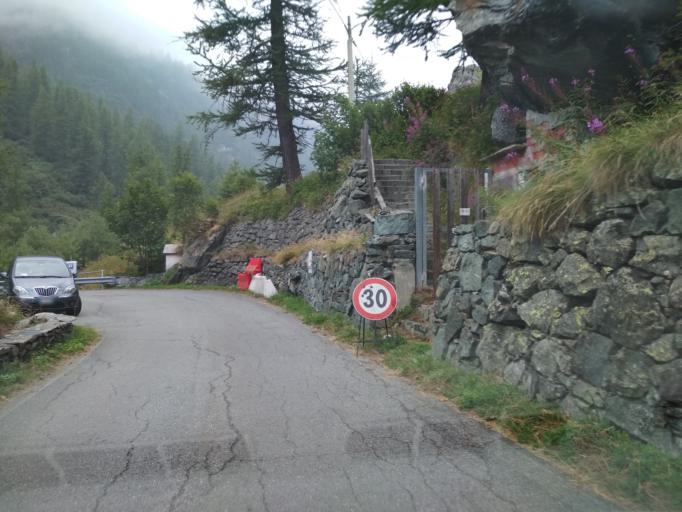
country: IT
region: Piedmont
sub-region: Provincia di Torino
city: Balme
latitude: 45.3026
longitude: 7.1930
